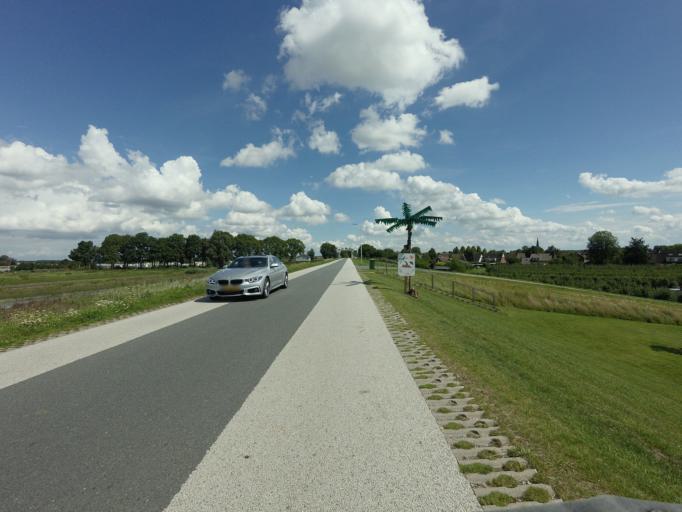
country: NL
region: Utrecht
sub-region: Gemeente IJsselstein
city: IJsselstein
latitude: 51.9657
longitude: 5.0283
